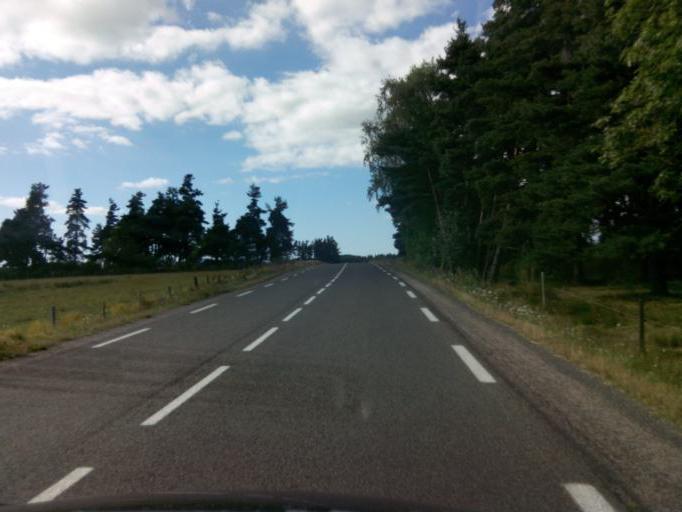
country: FR
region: Auvergne
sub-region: Departement de la Haute-Loire
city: Saint-Paulien
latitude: 45.1990
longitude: 3.8204
